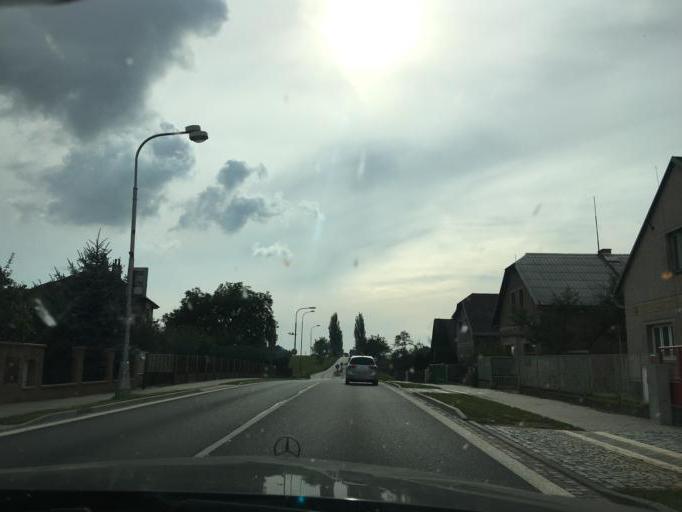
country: CZ
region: Kralovehradecky
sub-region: Okres Hradec Kralove
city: Smirice
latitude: 50.3073
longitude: 15.8573
